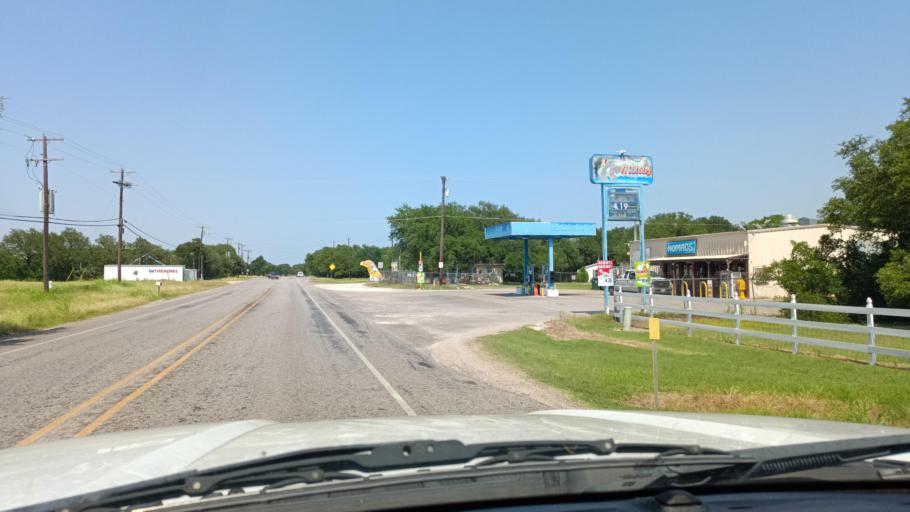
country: US
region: Texas
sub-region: Bell County
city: Belton
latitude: 31.1020
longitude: -97.4868
